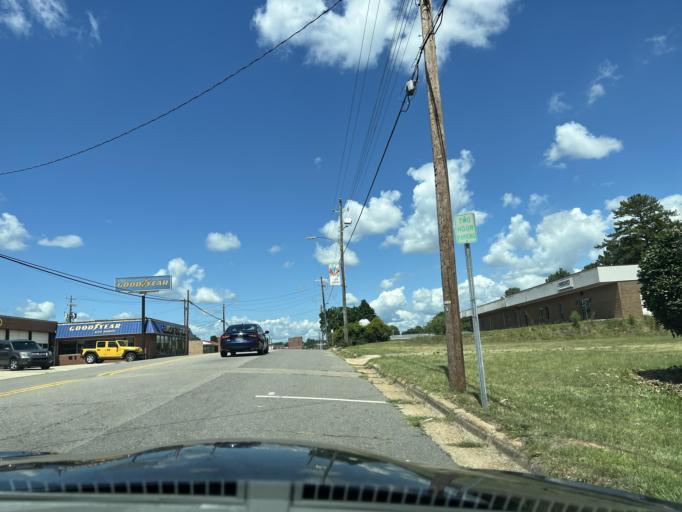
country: US
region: North Carolina
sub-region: Lee County
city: Sanford
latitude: 35.4750
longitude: -79.1860
